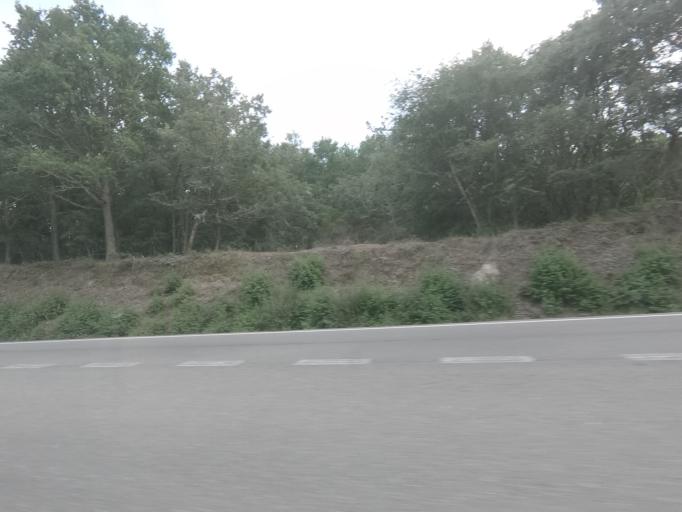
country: ES
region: Galicia
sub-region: Provincia de Ourense
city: Taboadela
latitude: 42.2196
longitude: -7.8404
